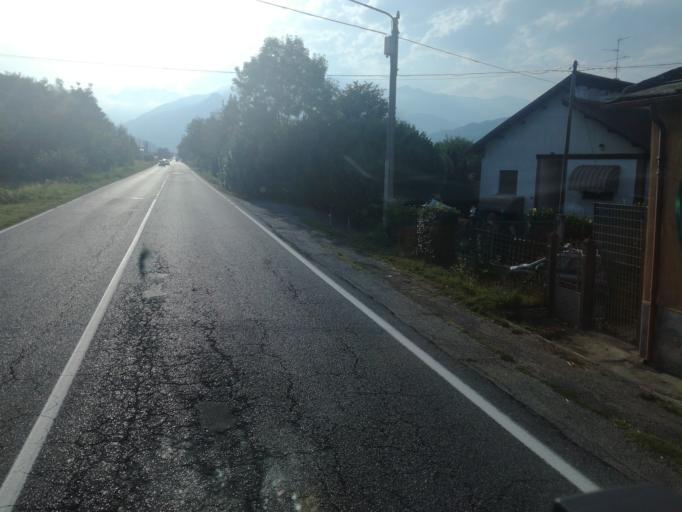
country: IT
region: Piedmont
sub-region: Provincia di Torino
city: Bibiana
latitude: 44.8103
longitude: 7.2809
